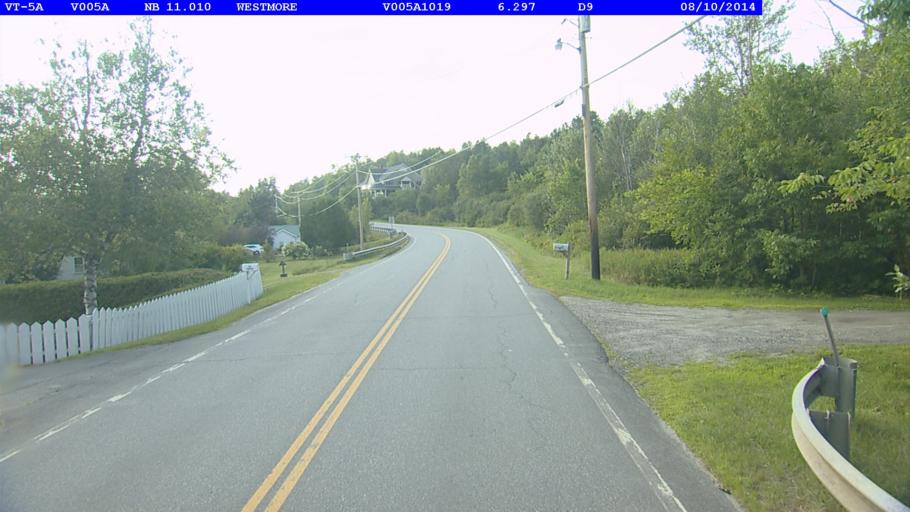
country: US
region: Vermont
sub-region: Orleans County
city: Newport
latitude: 44.7786
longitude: -72.0639
